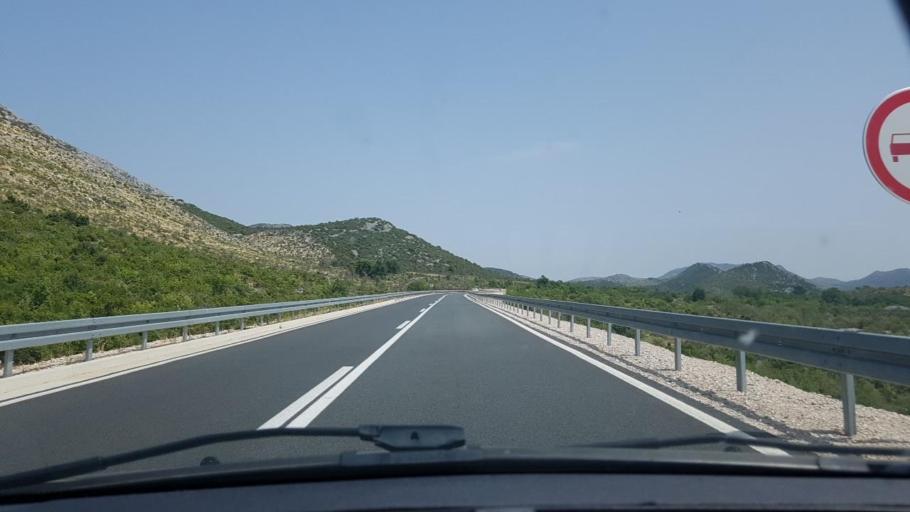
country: BA
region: Federation of Bosnia and Herzegovina
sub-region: Hercegovacko-Bosanski Kanton
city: Neum
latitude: 42.9561
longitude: 17.7301
